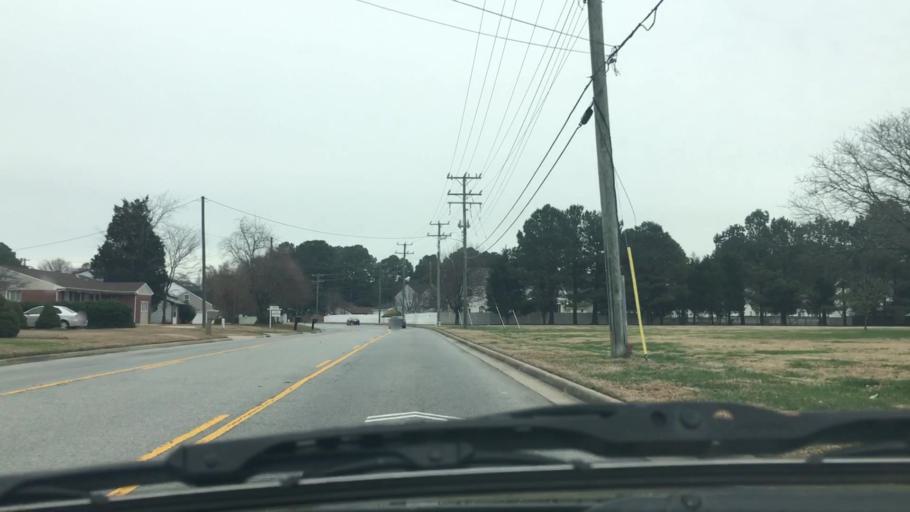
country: US
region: Virginia
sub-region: City of Portsmouth
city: Portsmouth Heights
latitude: 36.8592
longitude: -76.3772
